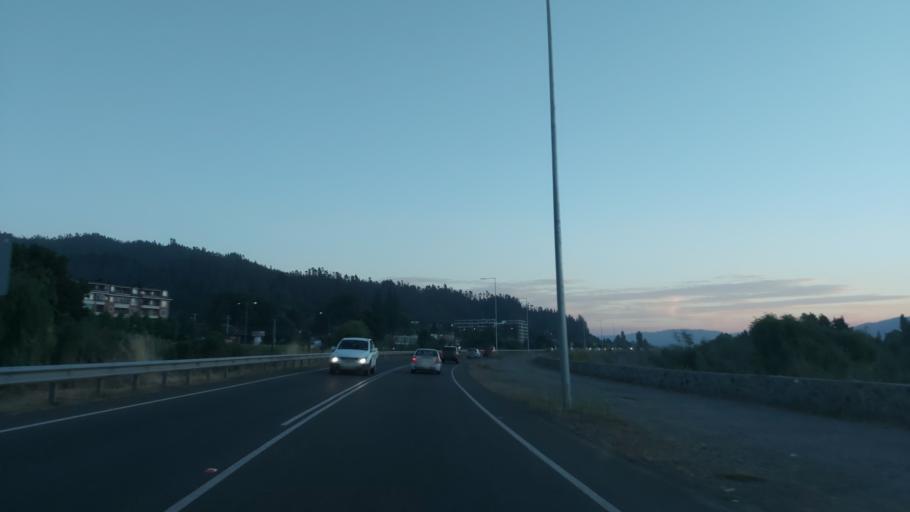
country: CL
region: Biobio
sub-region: Provincia de Concepcion
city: Chiguayante
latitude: -36.8775
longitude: -73.0396
